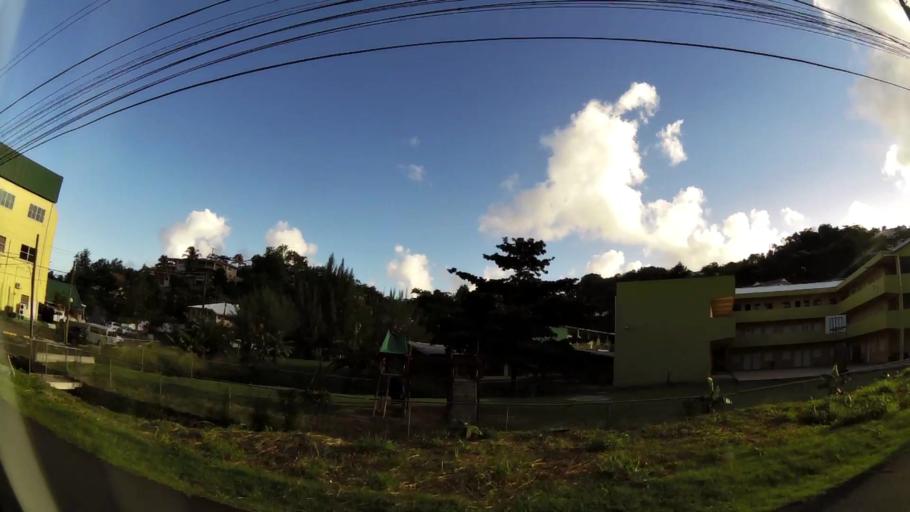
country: LC
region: Castries Quarter
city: Bisee
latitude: 14.0285
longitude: -60.9754
